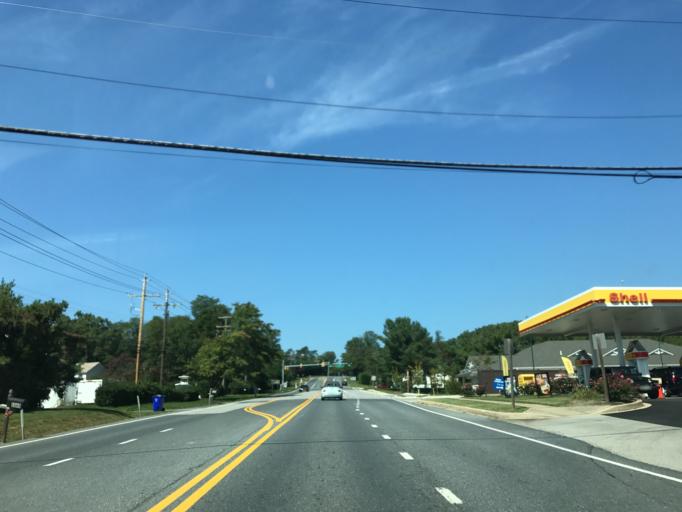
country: US
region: Maryland
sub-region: Howard County
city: Columbia
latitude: 39.2152
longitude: -76.8043
